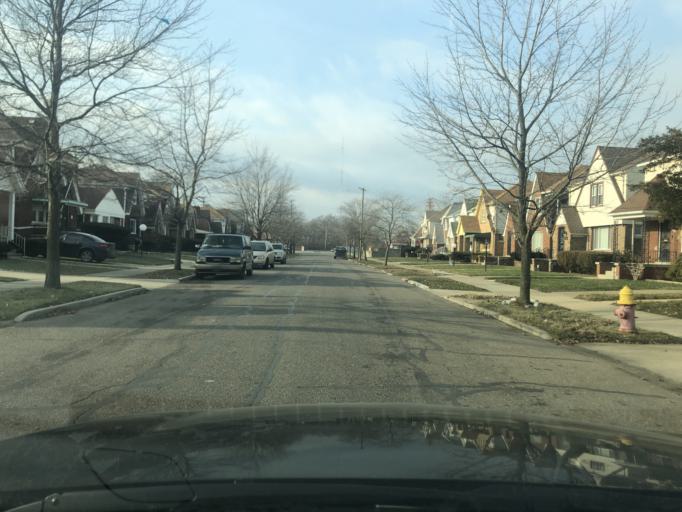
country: US
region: Michigan
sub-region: Wayne County
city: Highland Park
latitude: 42.3931
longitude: -83.1378
